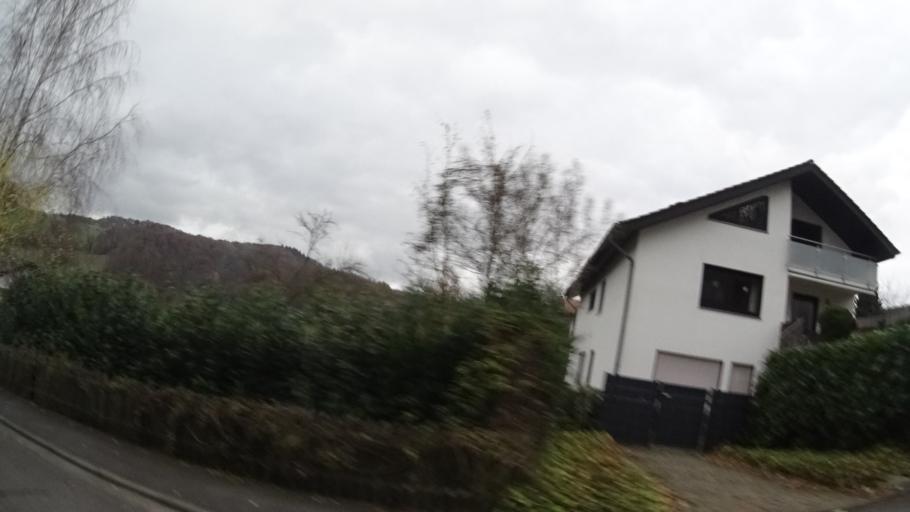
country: DE
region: Baden-Wuerttemberg
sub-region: Karlsruhe Region
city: Schriesheim
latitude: 49.5082
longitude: 8.7040
